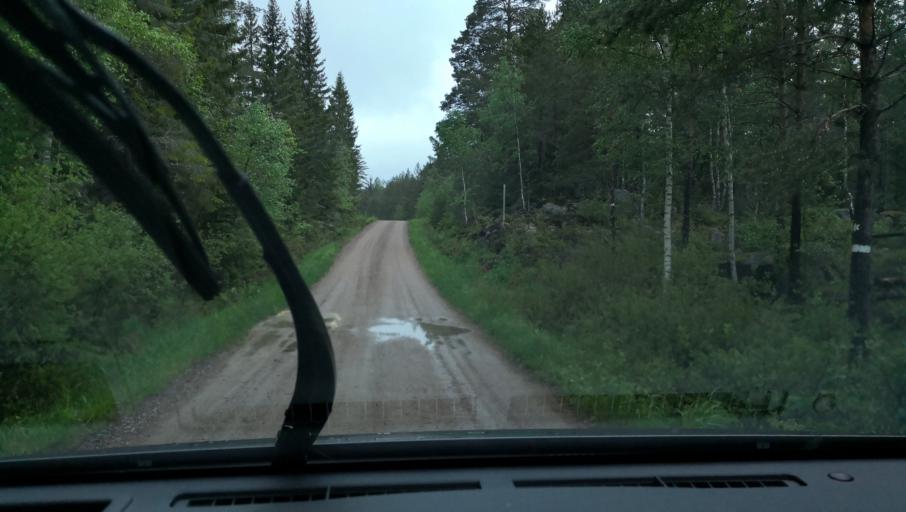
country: SE
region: Uppsala
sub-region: Enkopings Kommun
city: Orsundsbro
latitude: 59.9339
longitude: 17.3252
